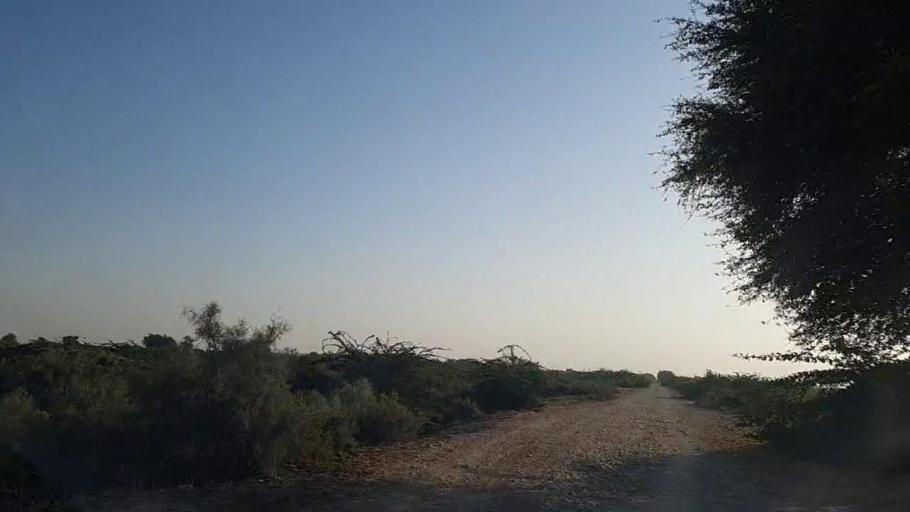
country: PK
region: Sindh
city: Jati
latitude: 24.4306
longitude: 68.1908
